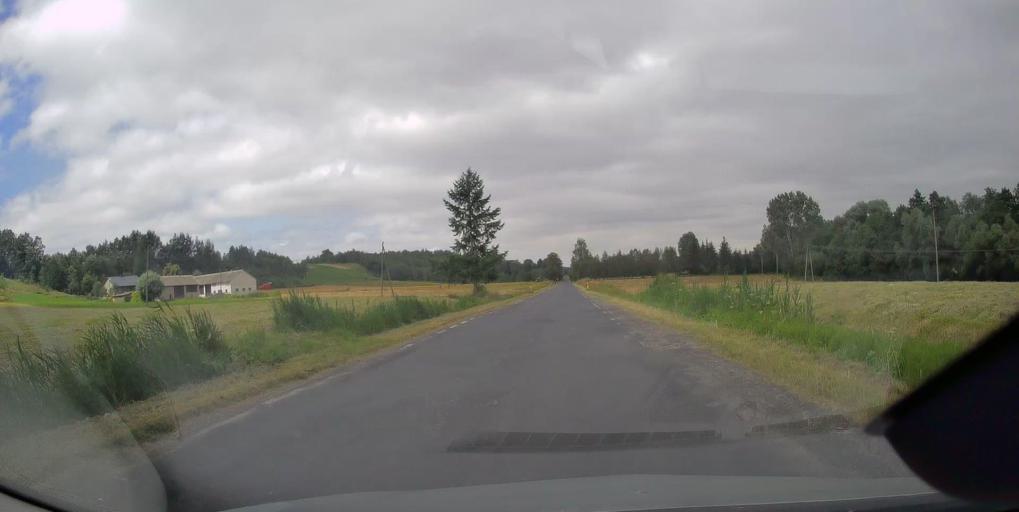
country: PL
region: Swietokrzyskie
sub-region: Powiat sandomierski
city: Klimontow
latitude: 50.6837
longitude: 21.3869
